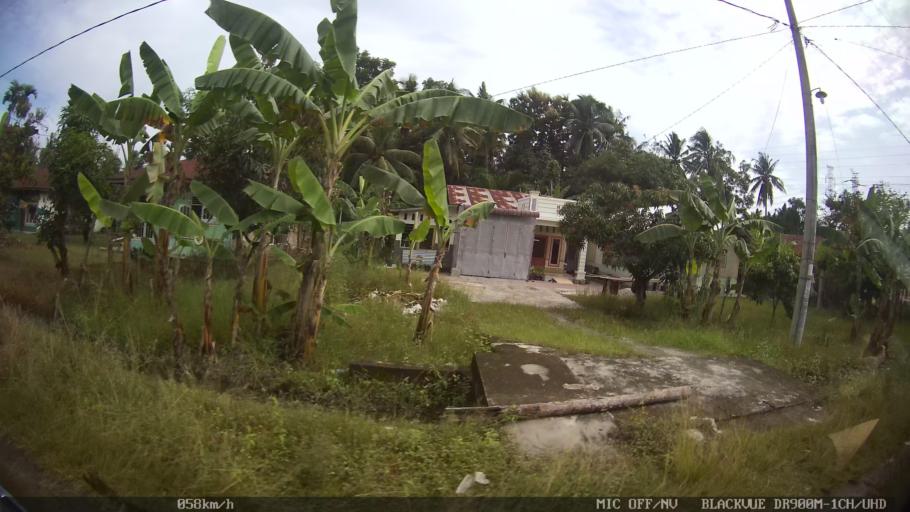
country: ID
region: North Sumatra
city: Percut
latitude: 3.6199
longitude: 98.7858
